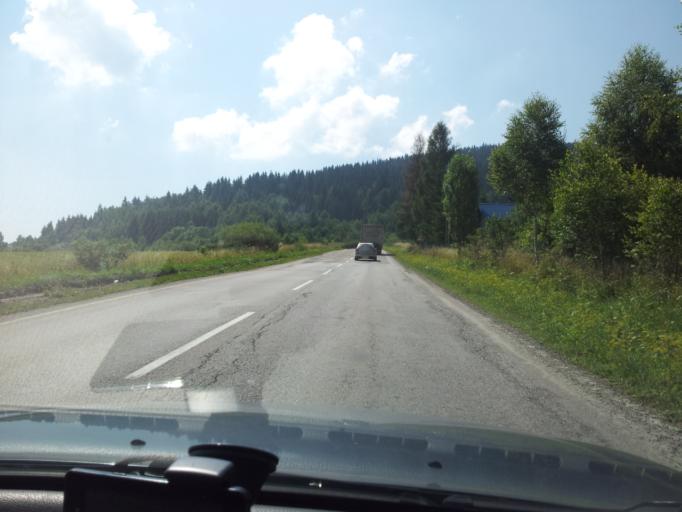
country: SK
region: Zilinsky
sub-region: Okres Dolny Kubin
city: Dolny Kubin
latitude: 49.3126
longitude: 19.3484
